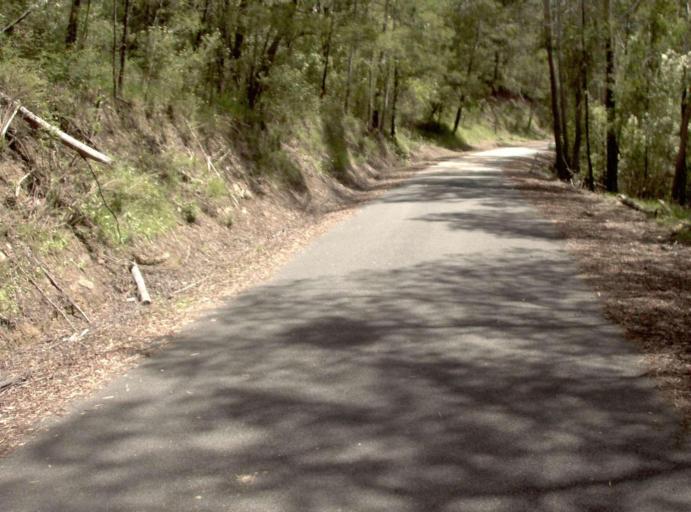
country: AU
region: New South Wales
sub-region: Bombala
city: Bombala
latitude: -37.4292
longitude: 149.0039
